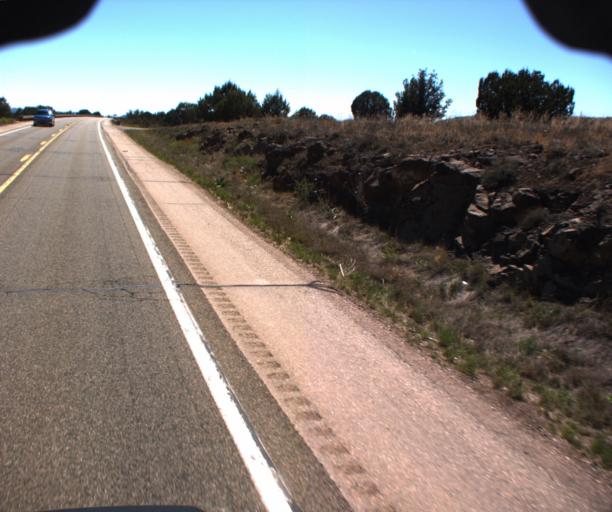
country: US
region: Arizona
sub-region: Yavapai County
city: Paulden
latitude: 34.9408
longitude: -112.4293
